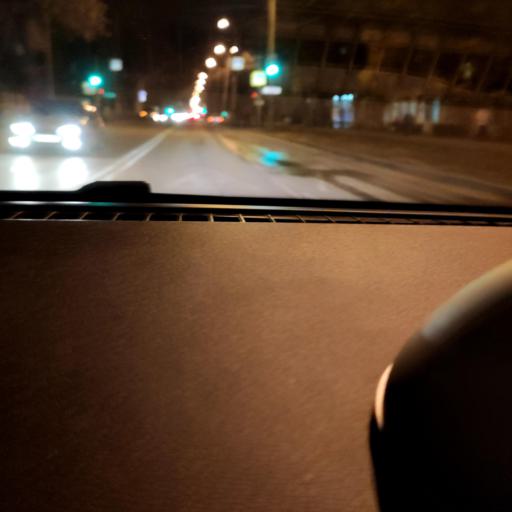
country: RU
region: Samara
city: Samara
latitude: 53.2079
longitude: 50.2425
